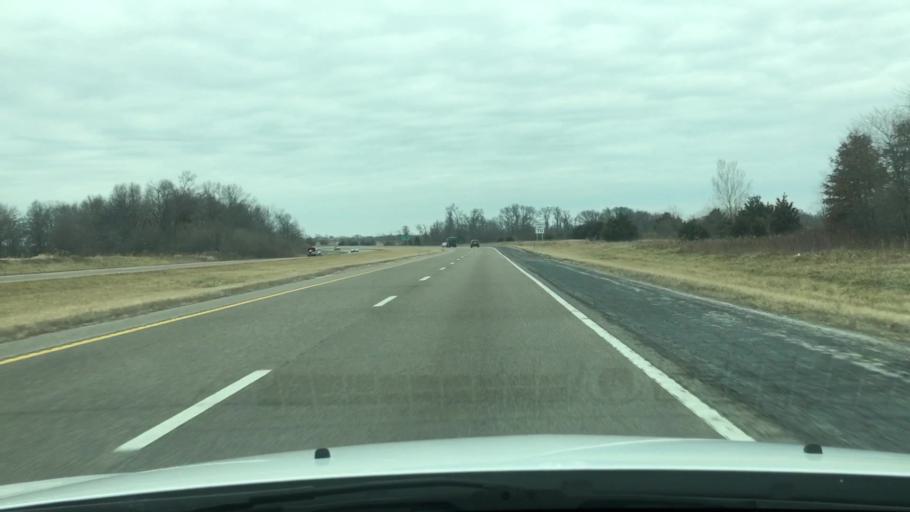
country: US
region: Missouri
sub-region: Audrain County
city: Mexico
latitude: 39.0261
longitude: -91.8855
